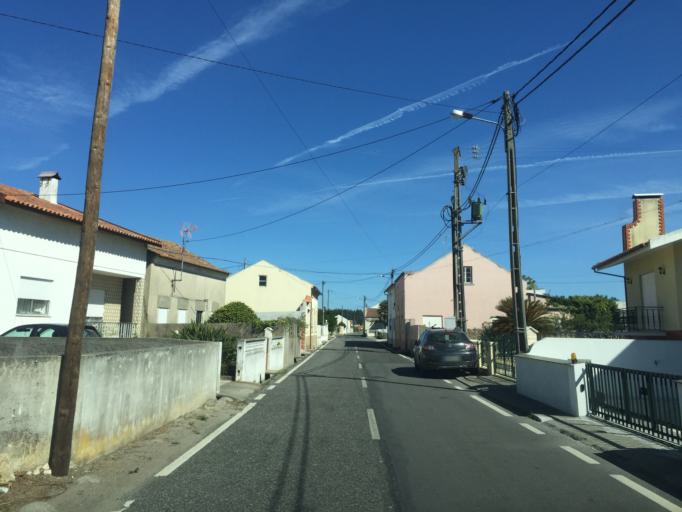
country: PT
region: Coimbra
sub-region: Figueira da Foz
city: Tavarede
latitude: 40.2146
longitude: -8.8467
